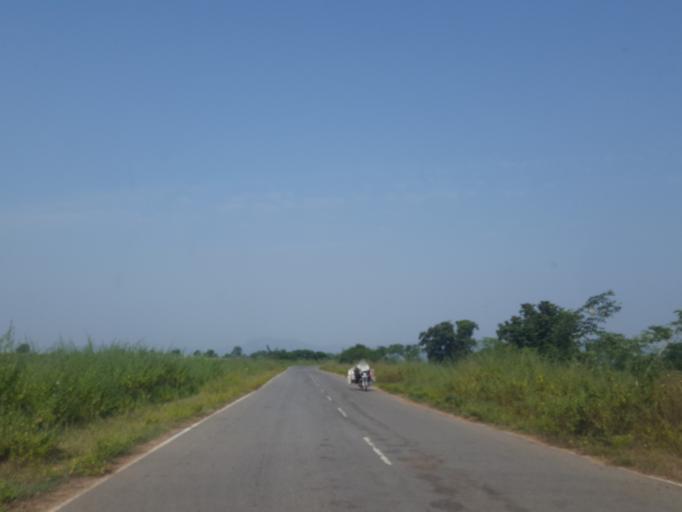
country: IN
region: Telangana
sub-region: Khammam
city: Yellandu
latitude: 17.6516
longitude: 80.2839
